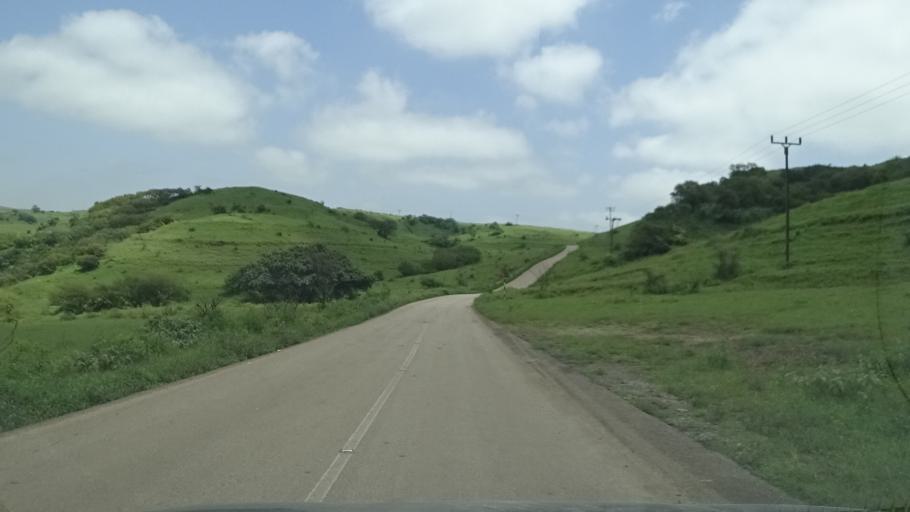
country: OM
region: Zufar
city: Salalah
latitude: 17.2141
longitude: 54.1950
